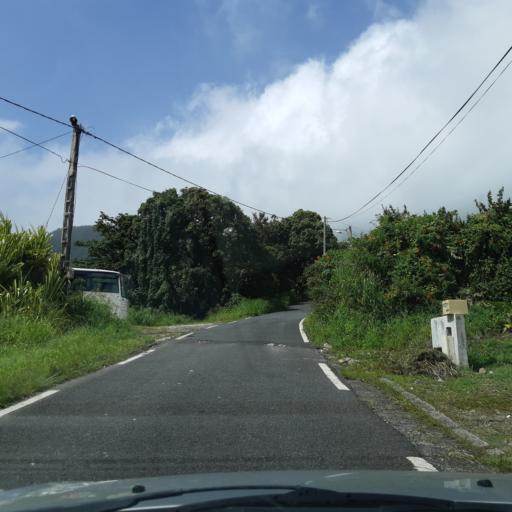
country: GP
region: Guadeloupe
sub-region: Guadeloupe
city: Saint-Claude
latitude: 16.0312
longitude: -61.6871
